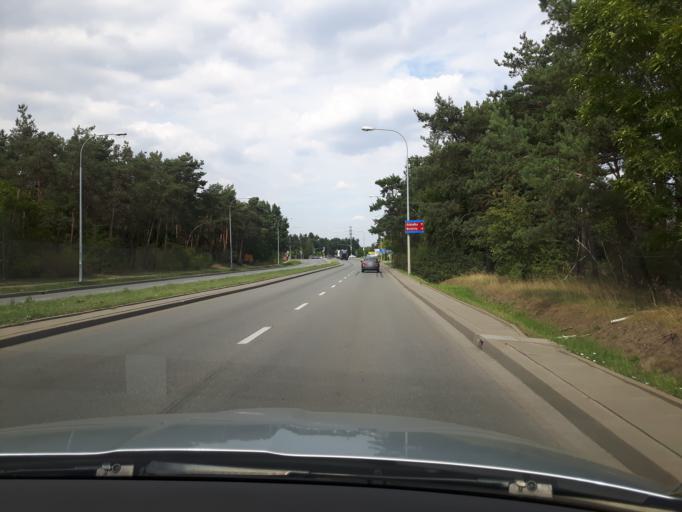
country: PL
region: Masovian Voivodeship
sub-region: Warszawa
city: Targowek
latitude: 52.3259
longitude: 21.0285
